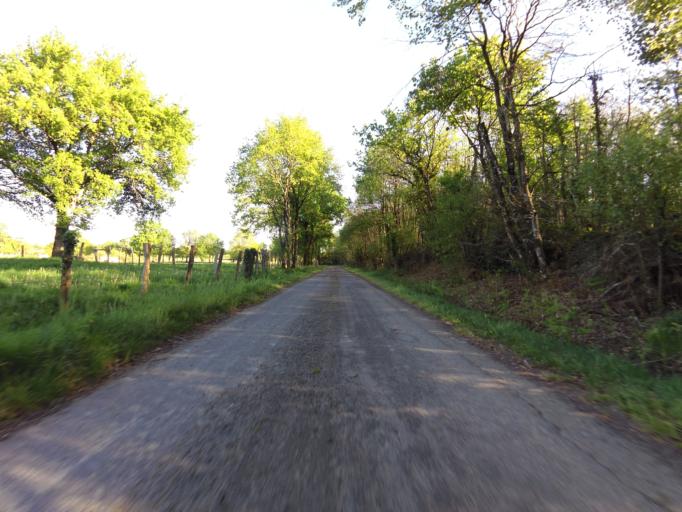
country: FR
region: Brittany
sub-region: Departement du Morbihan
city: Pluherlin
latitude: 47.7272
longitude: -2.3571
